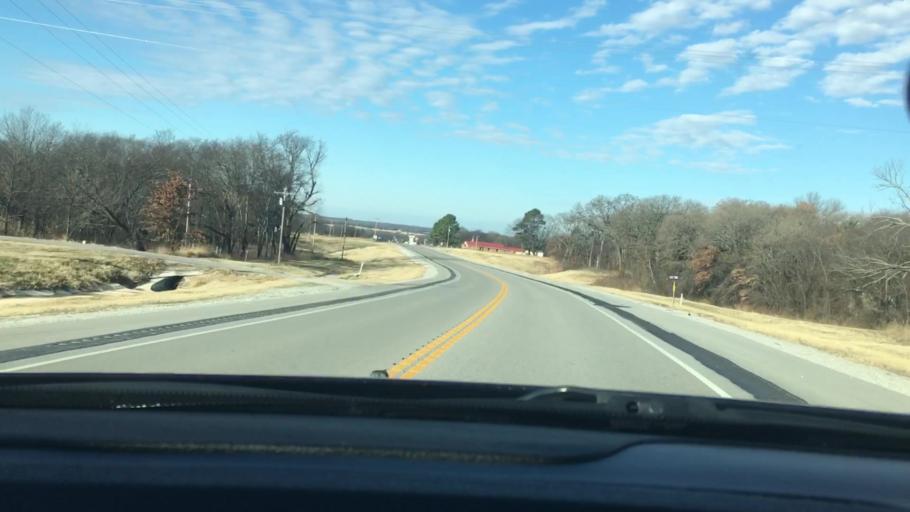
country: US
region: Oklahoma
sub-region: Love County
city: Marietta
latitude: 33.9400
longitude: -97.2742
